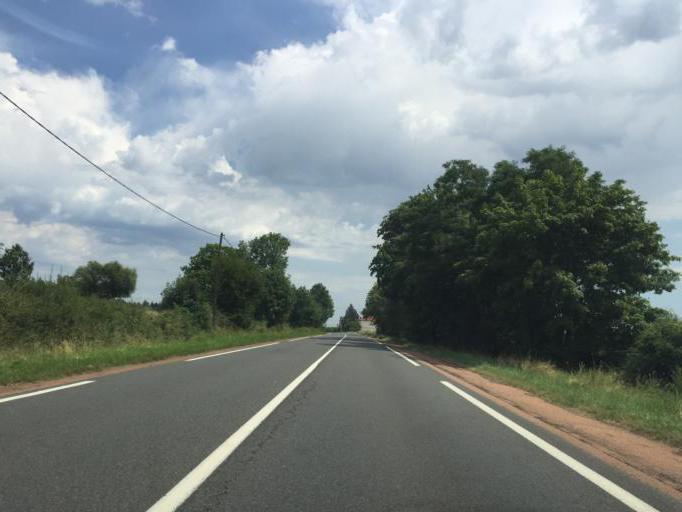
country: FR
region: Rhone-Alpes
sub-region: Departement du Rhone
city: Bully
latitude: 45.8571
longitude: 4.5674
